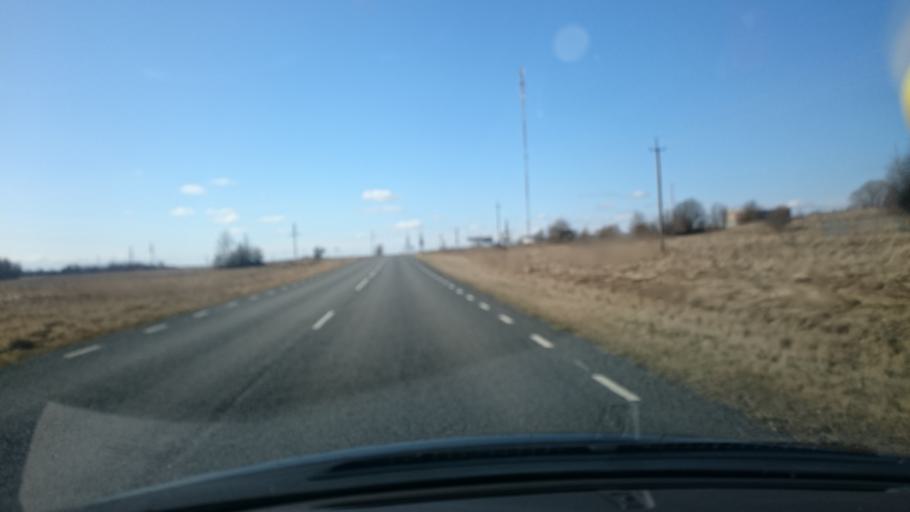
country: EE
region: Laeaene
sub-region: Lihula vald
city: Lihula
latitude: 58.6739
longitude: 23.8220
